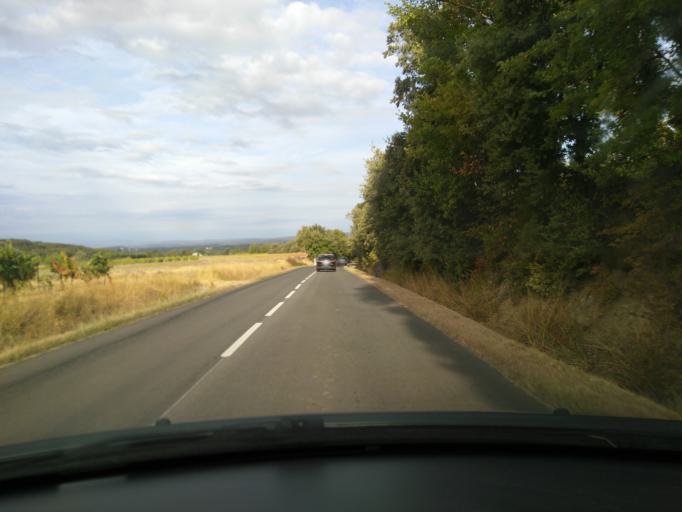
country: FR
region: Rhone-Alpes
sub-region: Departement de la Drome
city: Taulignan
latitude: 44.4280
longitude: 5.0319
